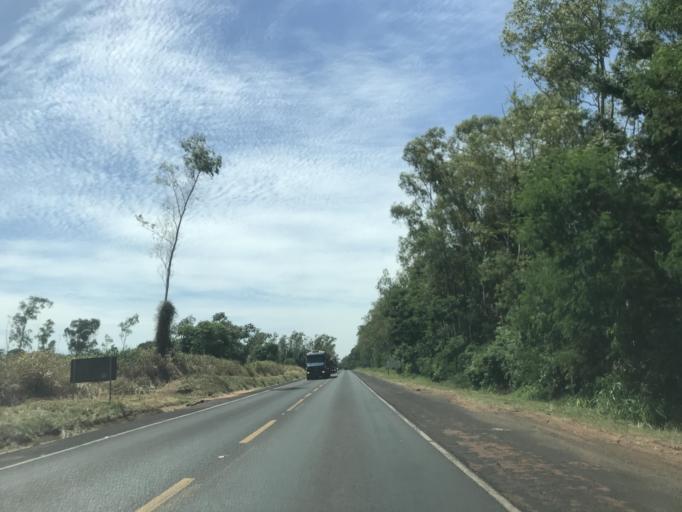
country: BR
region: Parana
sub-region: Paranavai
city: Nova Aurora
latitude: -22.9553
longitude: -52.6989
